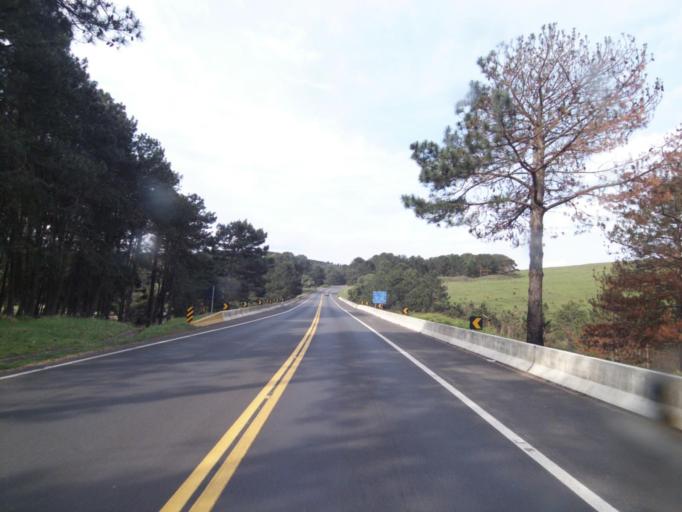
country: BR
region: Parana
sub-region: Campo Largo
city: Campo Largo
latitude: -25.4673
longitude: -49.7680
